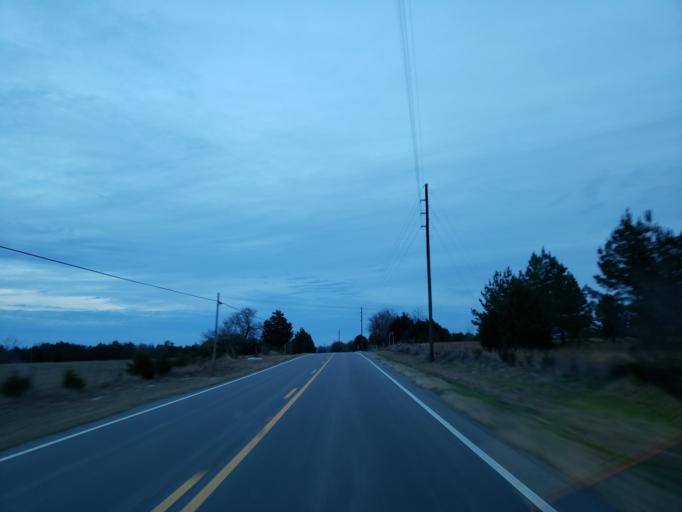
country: US
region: Alabama
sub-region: Sumter County
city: Livingston
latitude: 32.8114
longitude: -88.2711
